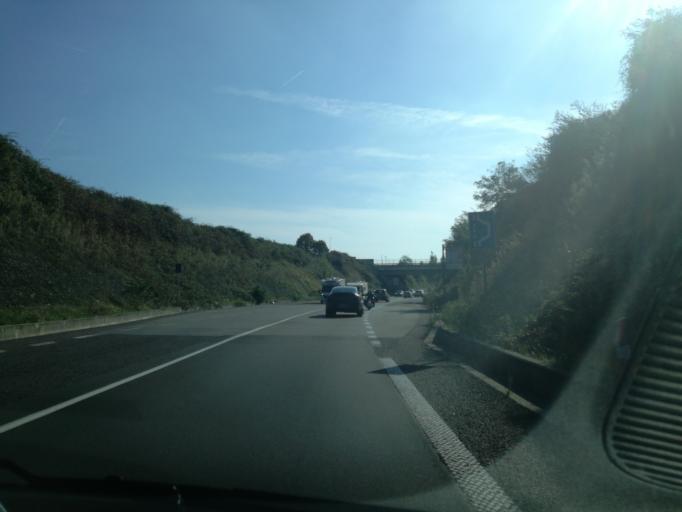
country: IT
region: Lombardy
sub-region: Provincia di Bergamo
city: Presezzo
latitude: 45.6993
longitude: 9.5603
